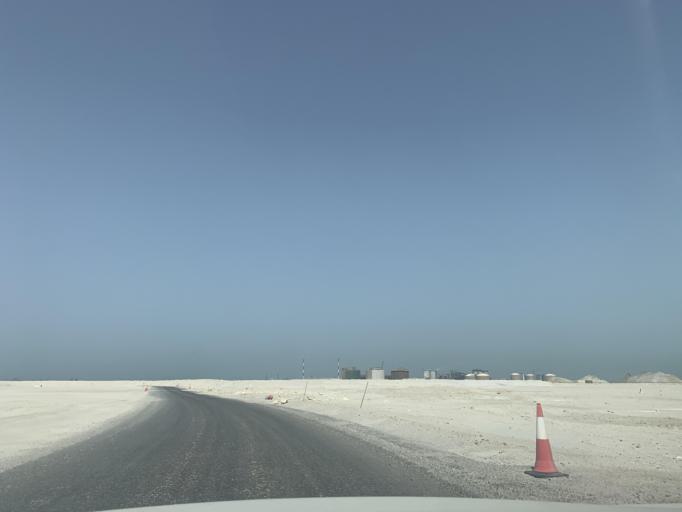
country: BH
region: Northern
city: Sitrah
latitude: 26.1581
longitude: 50.6403
